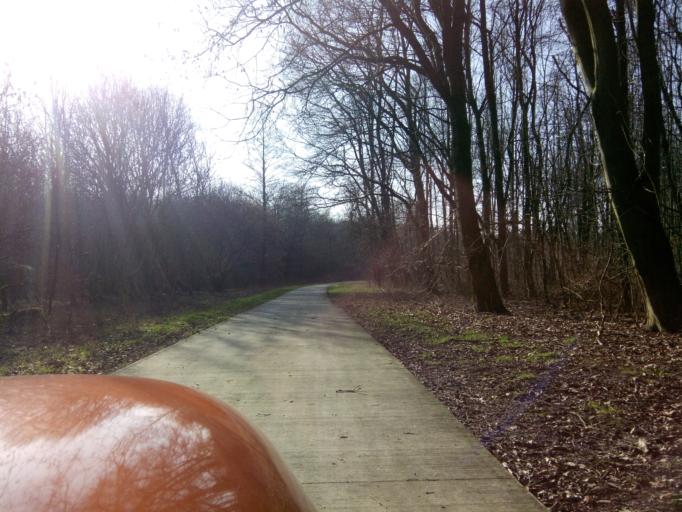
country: NL
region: Flevoland
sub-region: Gemeente Zeewolde
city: Zeewolde
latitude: 52.3314
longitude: 5.4945
